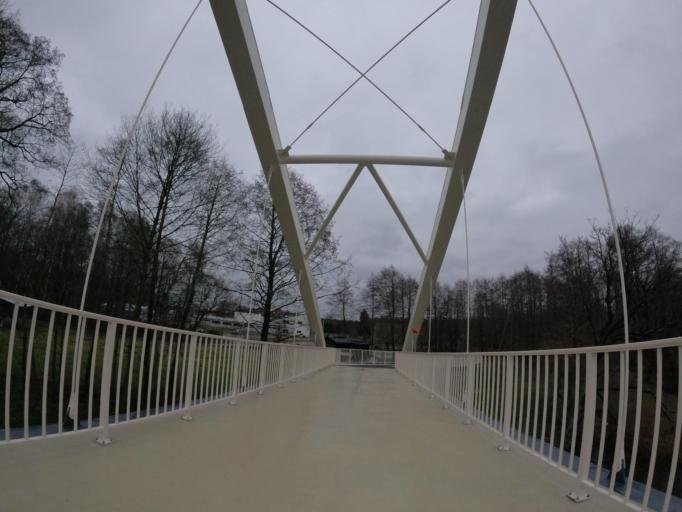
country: PL
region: Pomeranian Voivodeship
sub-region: Powiat slupski
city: Ustka
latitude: 54.5760
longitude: 16.8626
